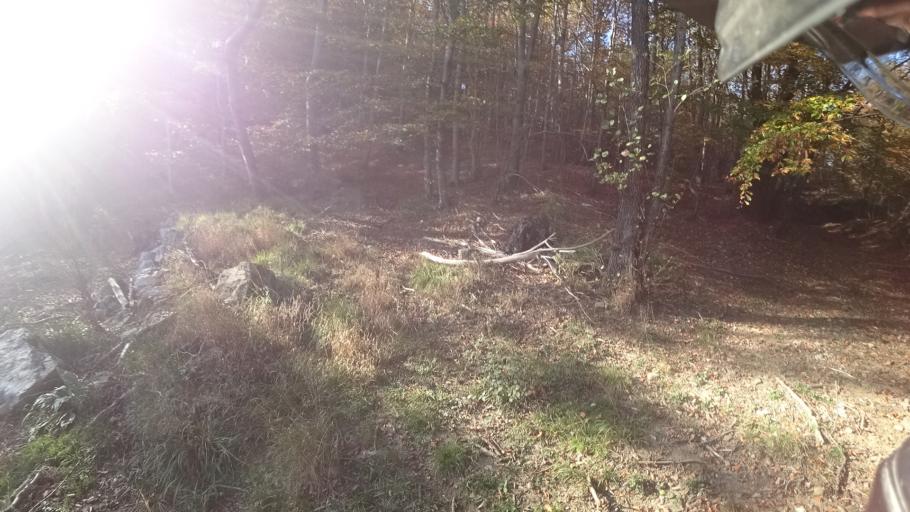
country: HR
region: Primorsko-Goranska
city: Klana
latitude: 45.4785
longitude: 14.3632
